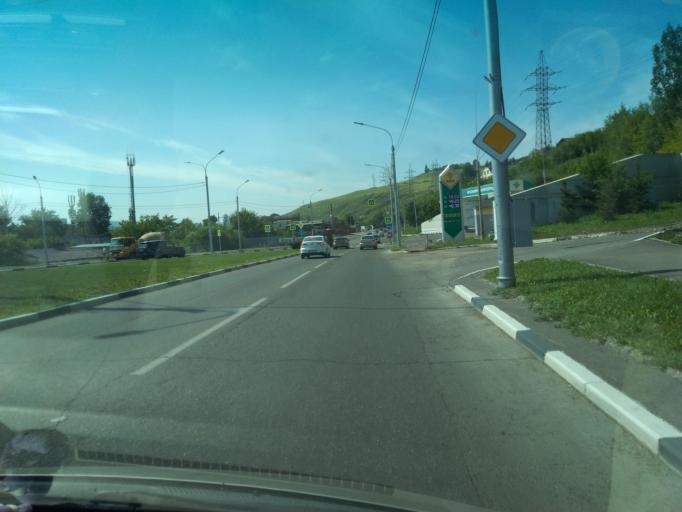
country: RU
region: Krasnoyarskiy
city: Krasnoyarsk
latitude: 56.0199
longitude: 92.8763
